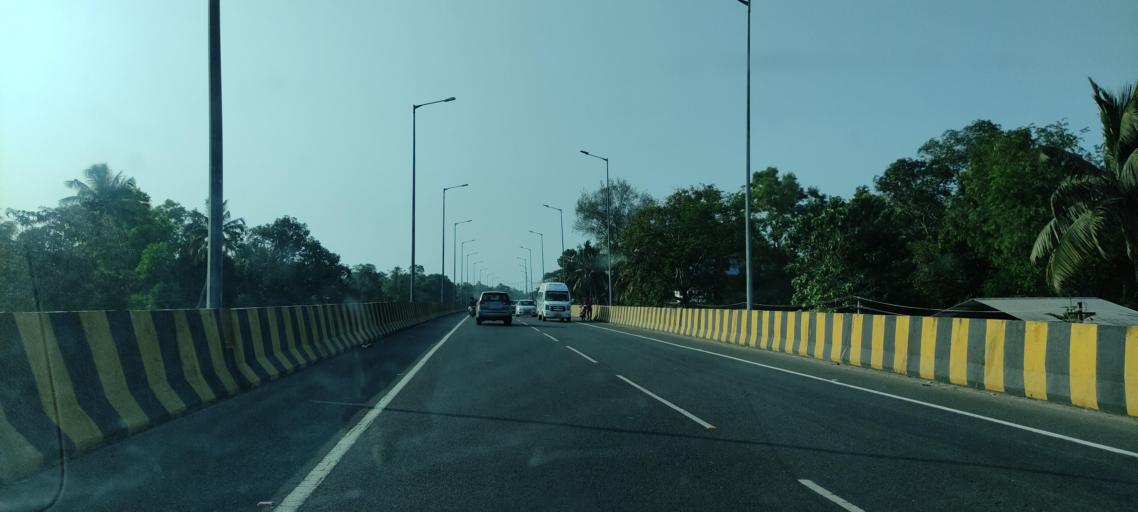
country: IN
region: Kerala
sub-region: Alappuzha
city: Alleppey
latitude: 9.4743
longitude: 76.3298
